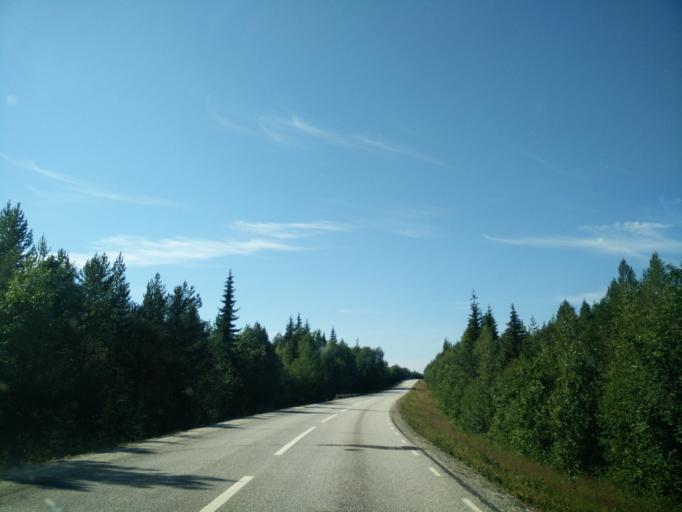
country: SE
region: Jaemtland
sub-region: Are Kommun
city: Jarpen
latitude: 62.7997
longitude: 13.5731
